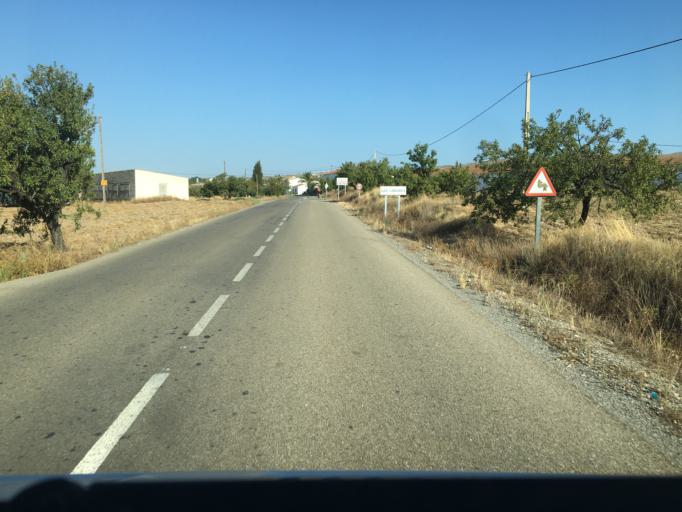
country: ES
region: Andalusia
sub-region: Provincia de Almeria
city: Huercal-Overa
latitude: 37.4686
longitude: -1.8905
